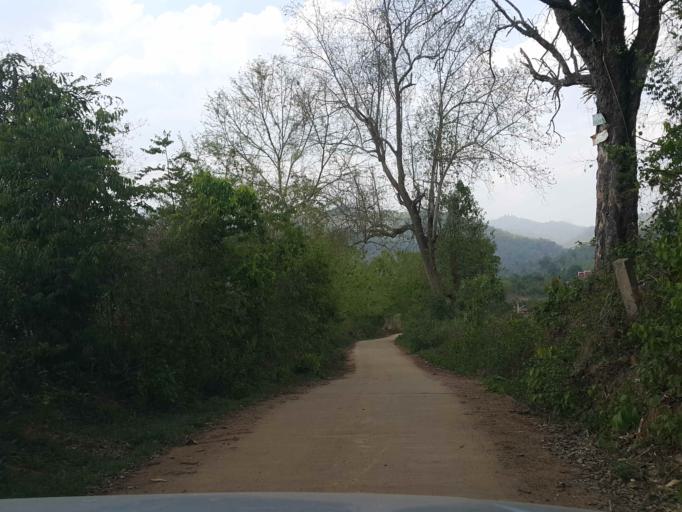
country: TH
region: Chiang Mai
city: Wiang Haeng
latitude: 19.3732
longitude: 98.7197
